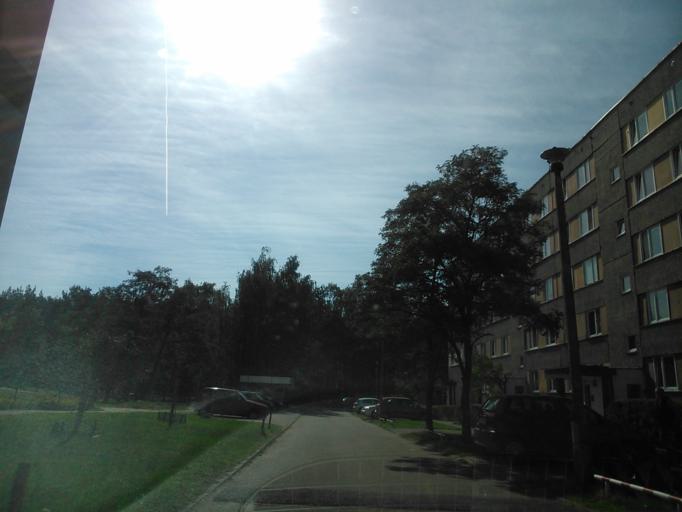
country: PL
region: Kujawsko-Pomorskie
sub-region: Powiat golubsko-dobrzynski
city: Golub-Dobrzyn
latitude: 53.1020
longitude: 19.0503
